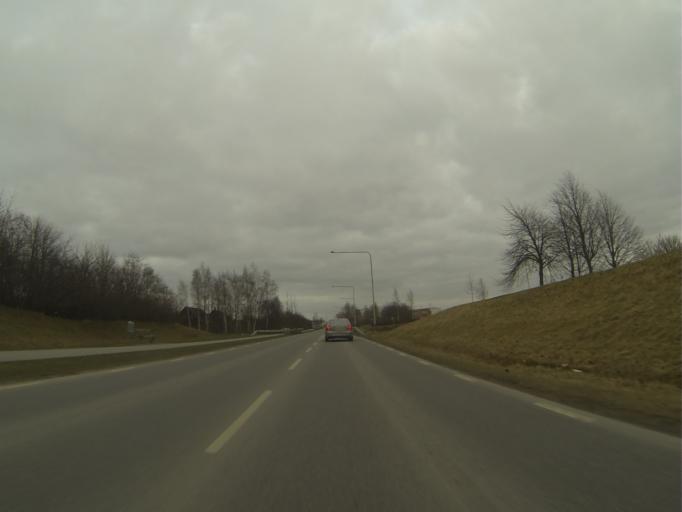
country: SE
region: Skane
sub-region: Svedala Kommun
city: Svedala
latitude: 55.5170
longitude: 13.2274
